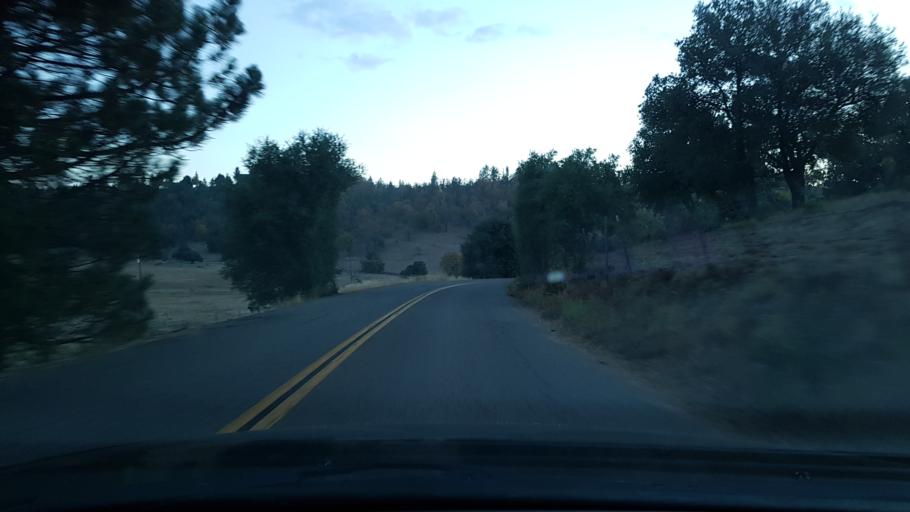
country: US
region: California
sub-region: San Diego County
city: Julian
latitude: 33.1003
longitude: -116.6108
